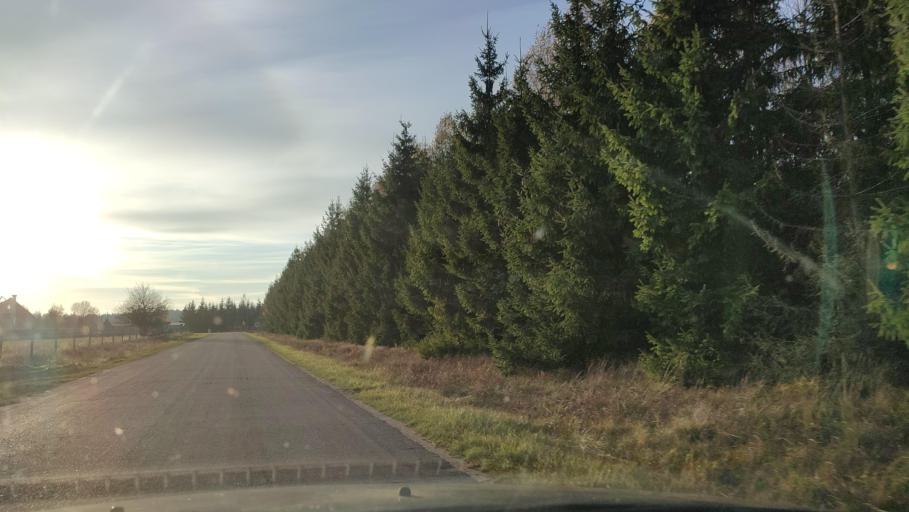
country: PL
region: Masovian Voivodeship
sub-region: Powiat mlawski
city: Dzierzgowo
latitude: 53.3249
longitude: 20.6763
